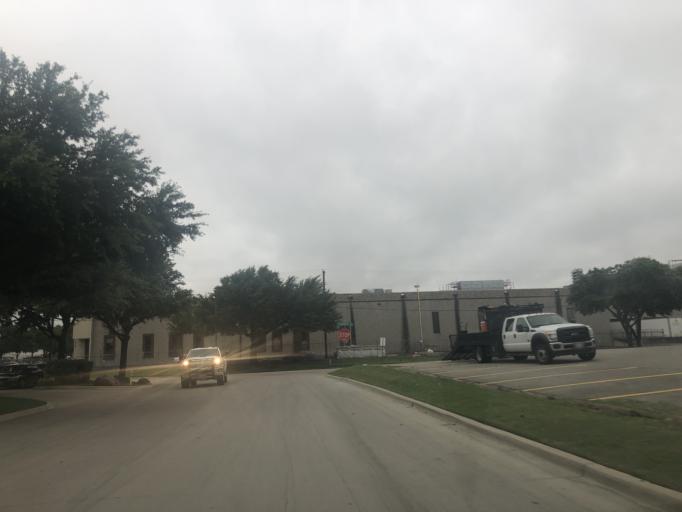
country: US
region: Texas
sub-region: Dallas County
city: Cockrell Hill
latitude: 32.7733
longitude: -96.8585
